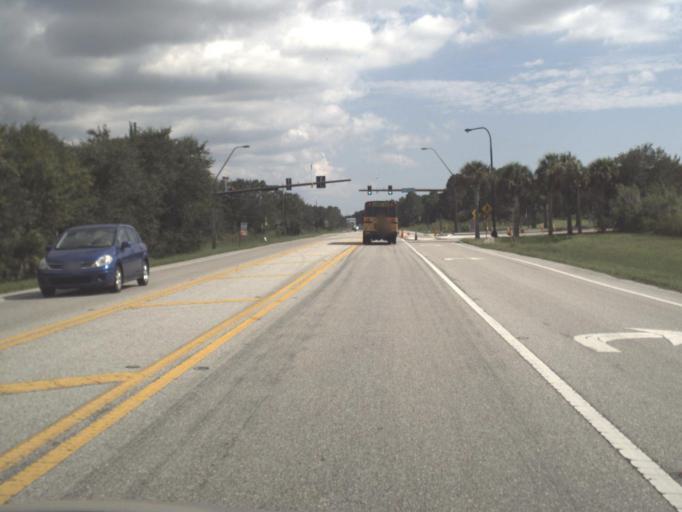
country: US
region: Florida
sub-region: Sarasota County
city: Plantation
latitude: 27.0804
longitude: -82.3313
